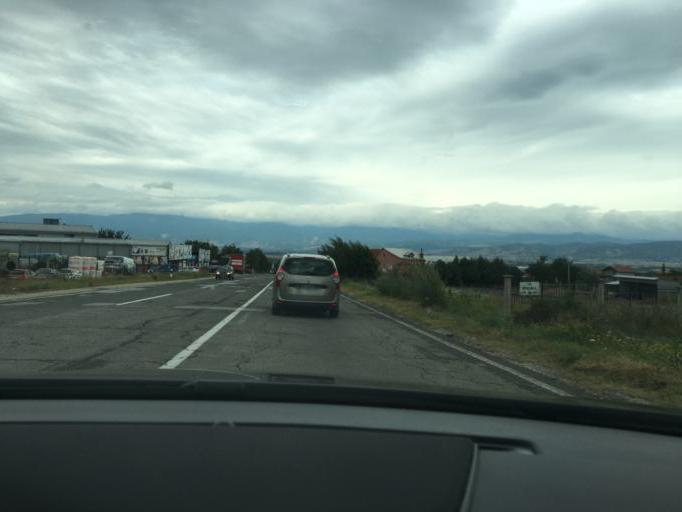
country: MK
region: Kumanovo
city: Kumanovo
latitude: 42.1632
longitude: 21.7515
